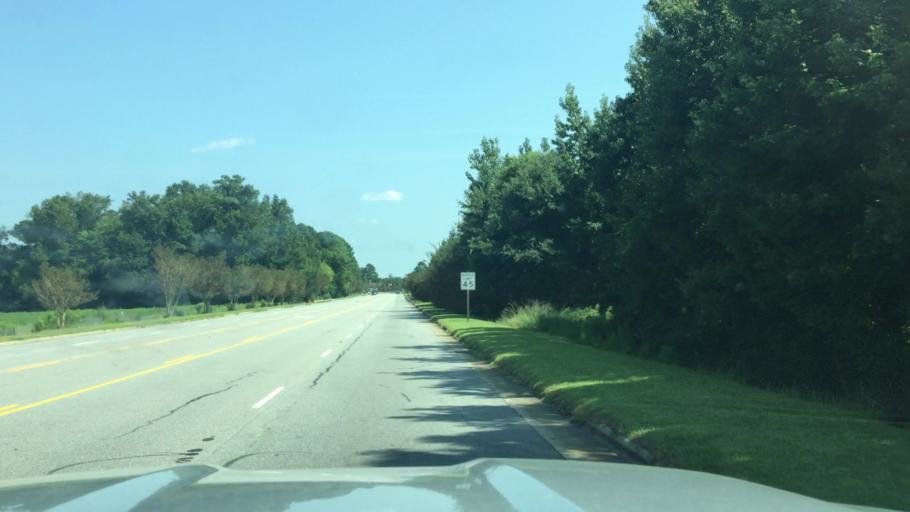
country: US
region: North Carolina
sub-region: Martin County
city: Williamston
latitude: 35.8092
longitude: -76.9064
